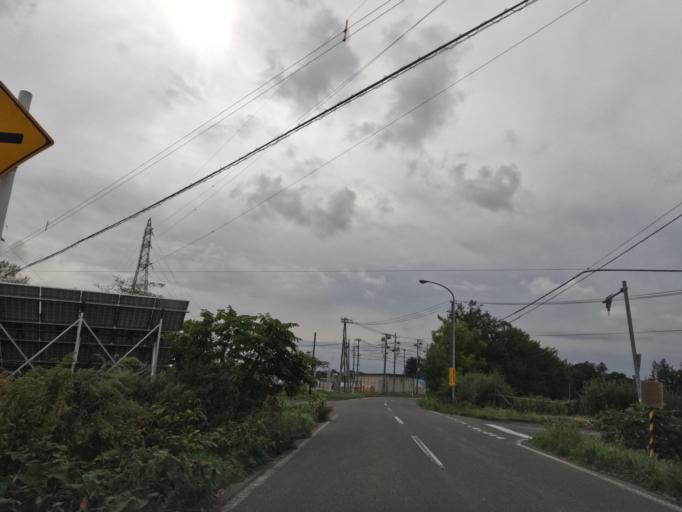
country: JP
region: Hokkaido
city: Date
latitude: 42.4595
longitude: 140.9033
